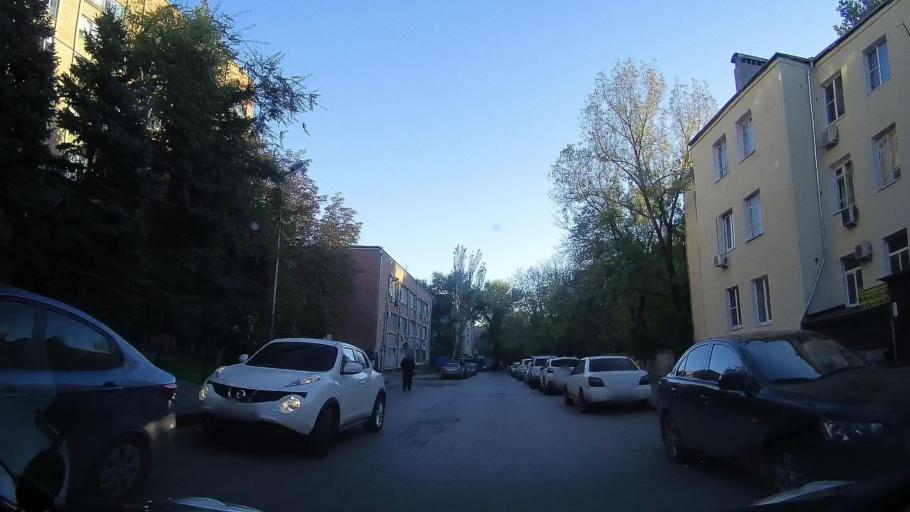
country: RU
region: Rostov
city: Rostov-na-Donu
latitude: 47.2383
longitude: 39.7027
